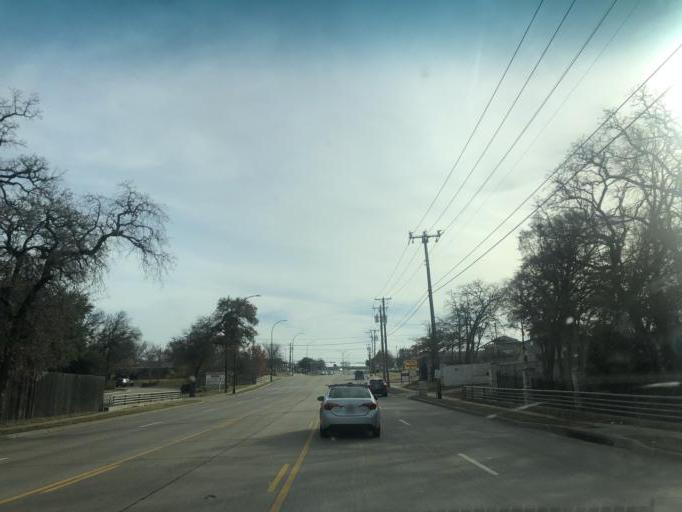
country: US
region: Texas
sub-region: Tarrant County
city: Dalworthington Gardens
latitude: 32.6802
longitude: -97.1496
